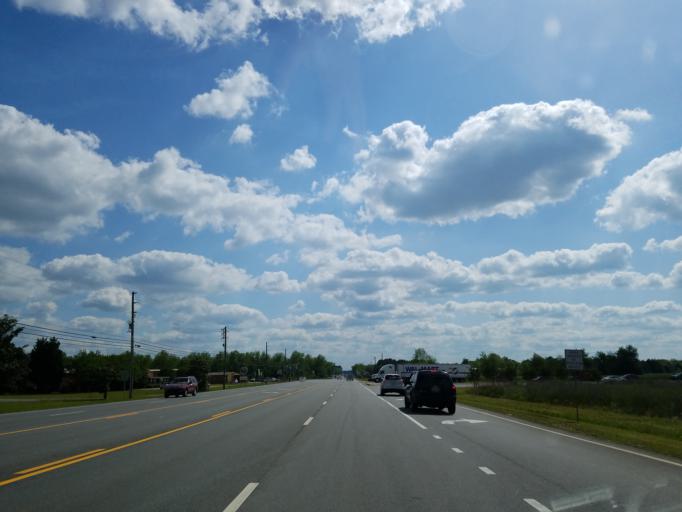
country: US
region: Georgia
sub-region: Peach County
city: Fort Valley
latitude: 32.5772
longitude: -83.8669
